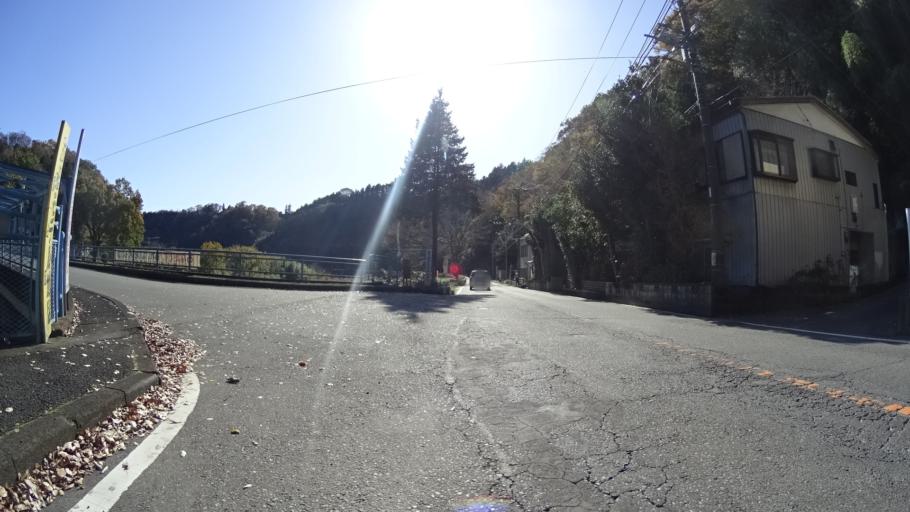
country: JP
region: Kanagawa
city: Zama
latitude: 35.5399
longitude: 139.2783
